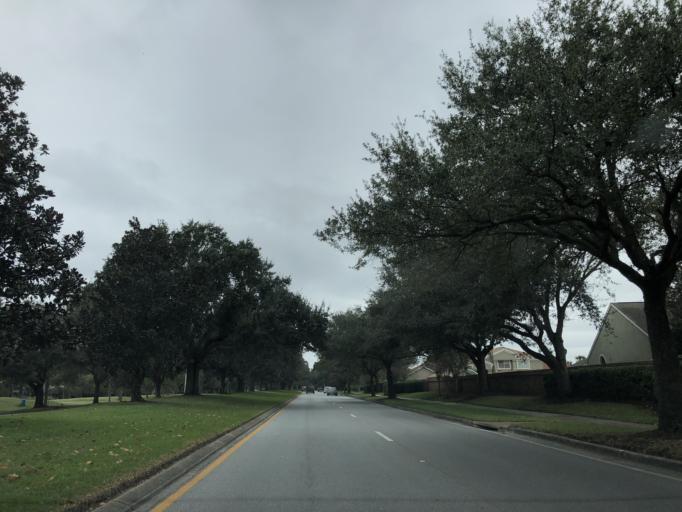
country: US
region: Florida
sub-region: Orange County
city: Hunters Creek
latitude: 28.3678
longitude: -81.4085
